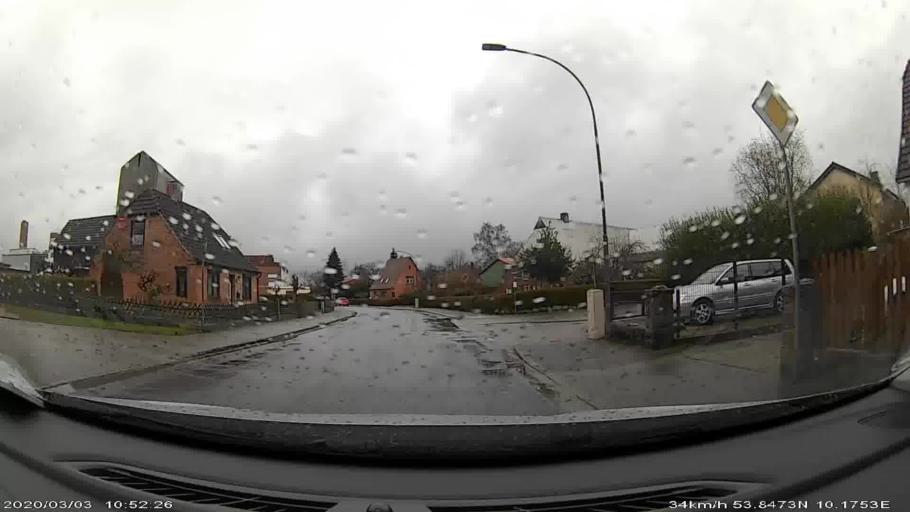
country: DE
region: Schleswig-Holstein
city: Seth
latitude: 53.8490
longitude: 10.1753
